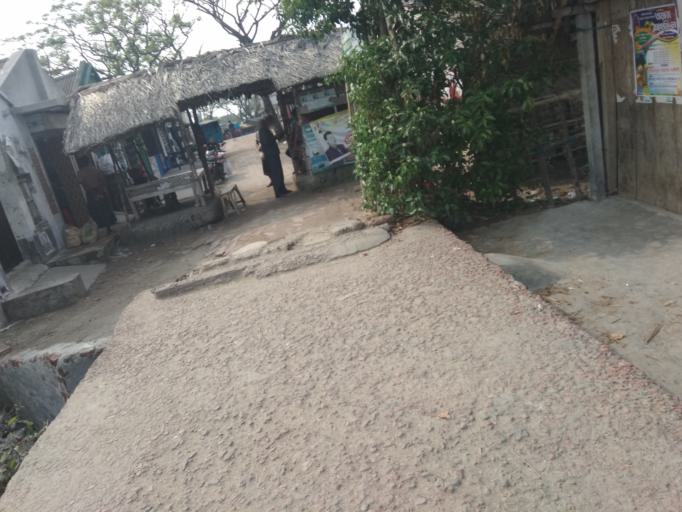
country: IN
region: West Bengal
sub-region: North 24 Parganas
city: Taki
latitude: 22.3475
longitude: 89.2034
